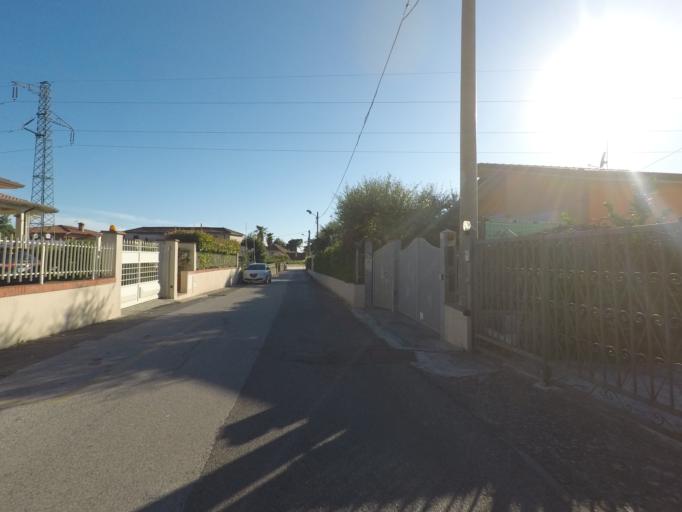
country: IT
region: Tuscany
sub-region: Provincia di Massa-Carrara
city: Capanne-Prato-Cinquale
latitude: 44.0079
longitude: 10.1555
